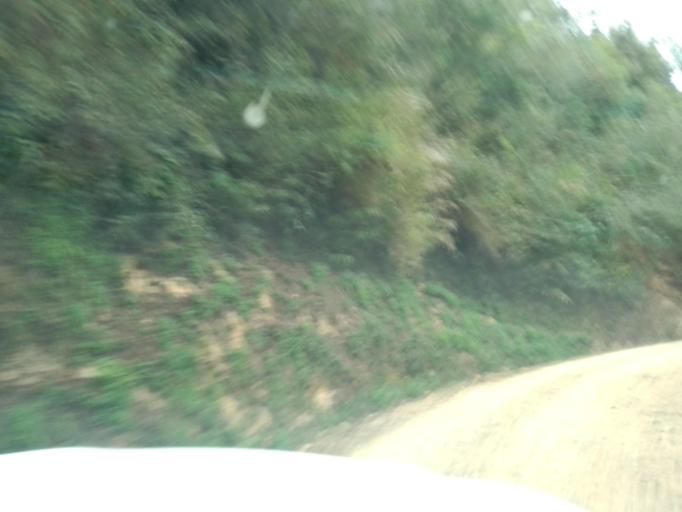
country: GT
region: San Marcos
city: Tacana
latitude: 15.2180
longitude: -92.2168
